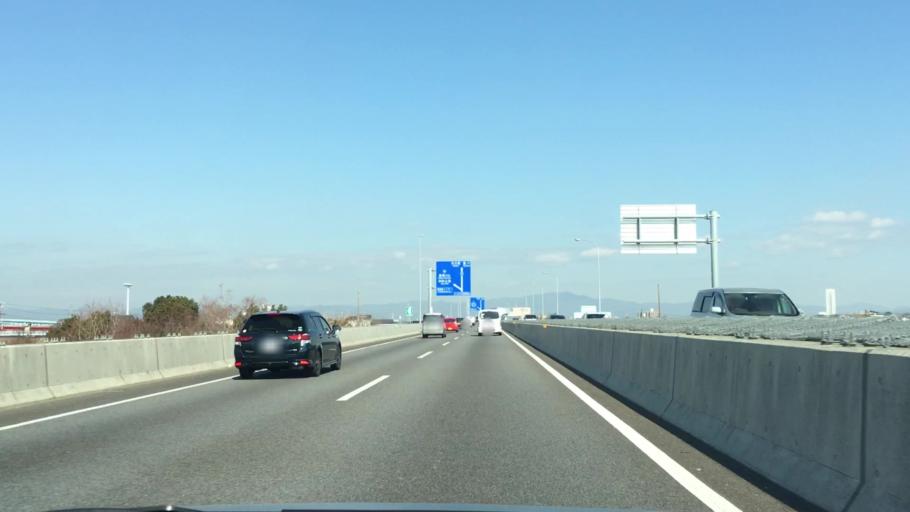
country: JP
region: Aichi
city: Toyohashi
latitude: 34.7200
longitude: 137.3536
